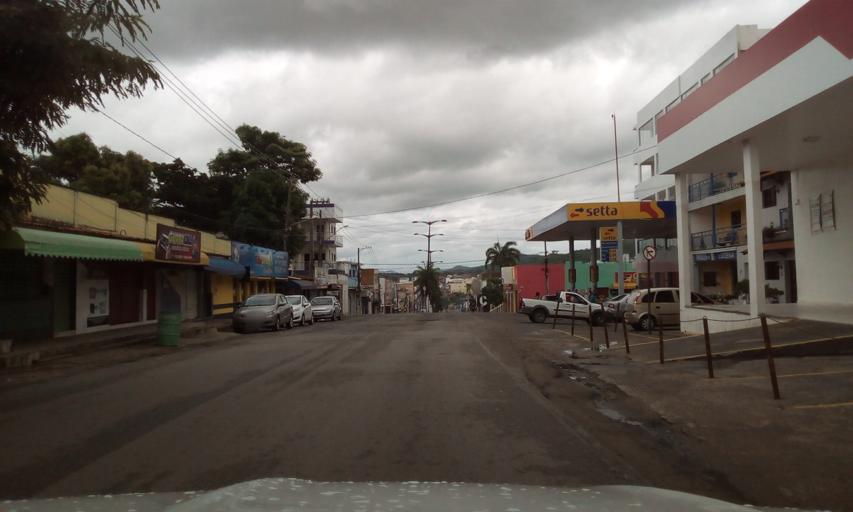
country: BR
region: Paraiba
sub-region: Guarabira
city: Guarabira
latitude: -6.8483
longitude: -35.4894
